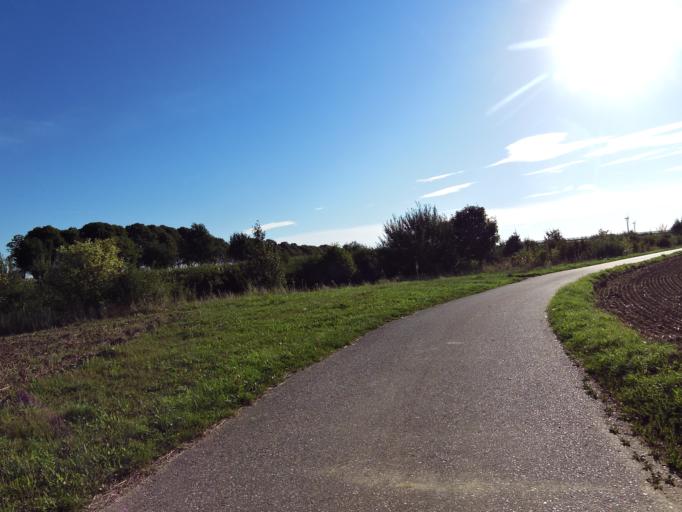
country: DE
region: North Rhine-Westphalia
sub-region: Regierungsbezirk Koln
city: Alsdorf
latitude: 50.8967
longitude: 6.1394
